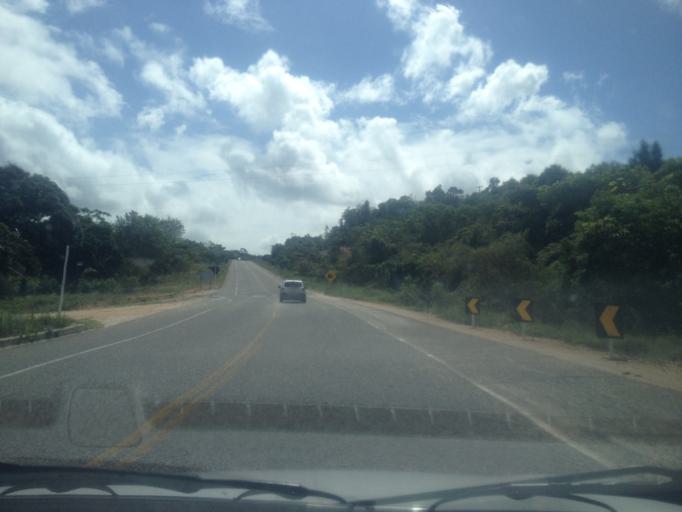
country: BR
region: Bahia
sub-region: Conde
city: Conde
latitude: -11.9781
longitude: -37.6751
